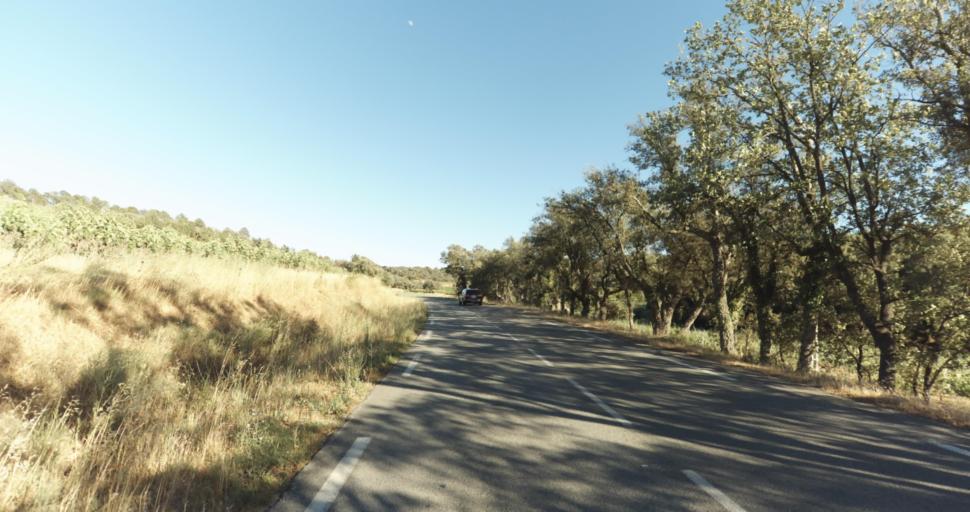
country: FR
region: Provence-Alpes-Cote d'Azur
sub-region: Departement du Var
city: Gassin
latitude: 43.2414
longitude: 6.5978
